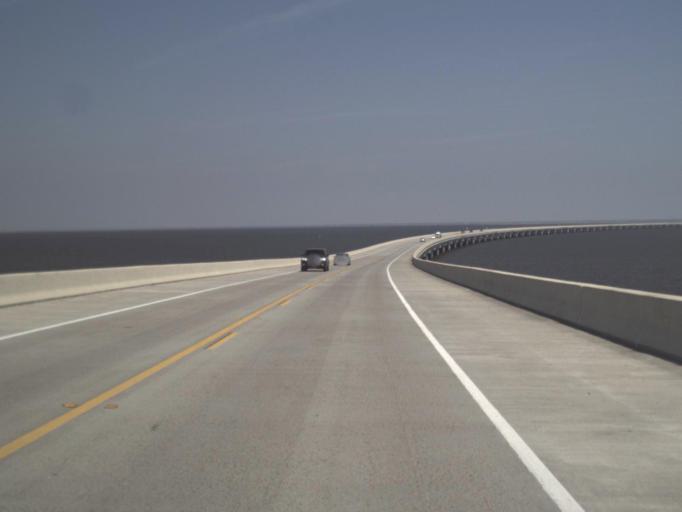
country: US
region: Florida
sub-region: Franklin County
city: Eastpoint
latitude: 29.6873
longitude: -84.8839
